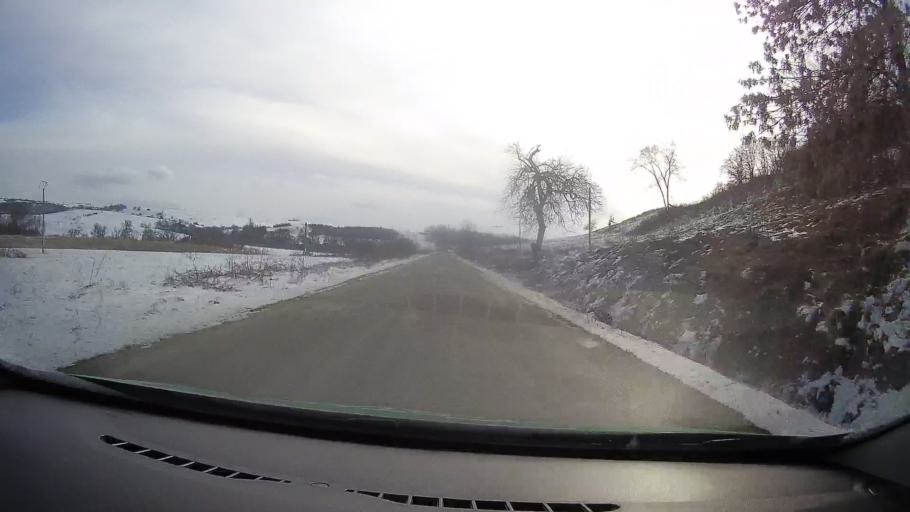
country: RO
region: Sibiu
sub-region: Comuna Iacobeni
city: Iacobeni
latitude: 46.0189
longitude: 24.6961
